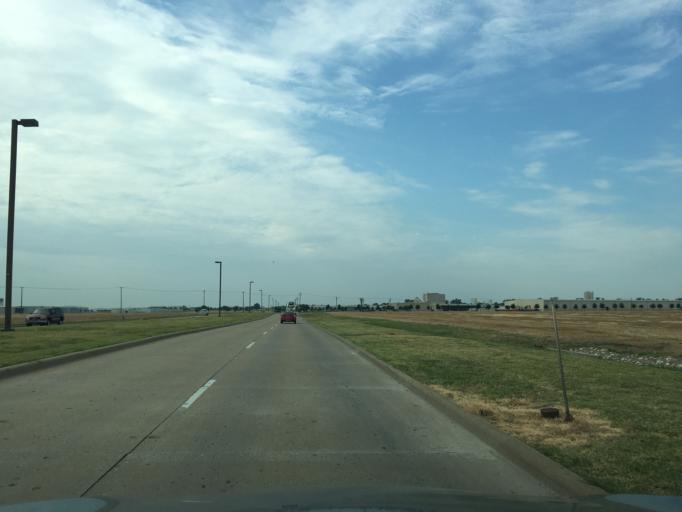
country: US
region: Texas
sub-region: Collin County
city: McKinney
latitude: 33.1887
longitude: -96.5981
